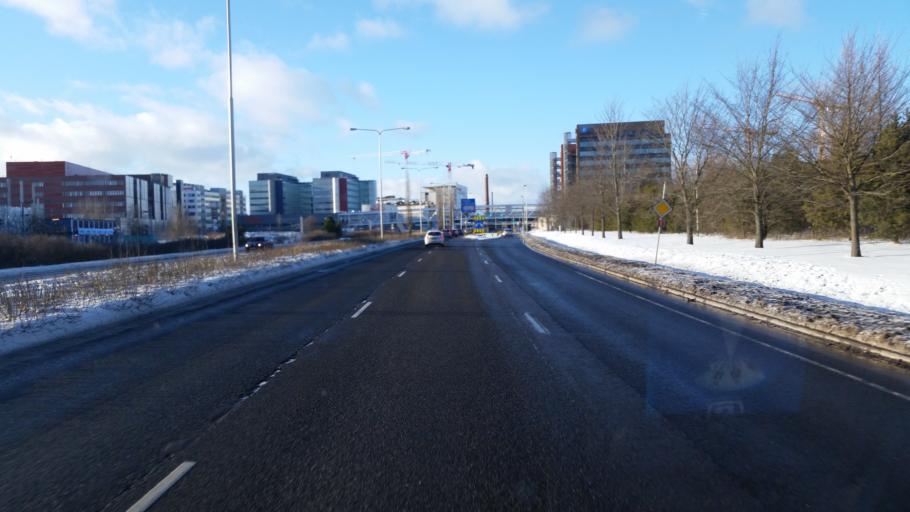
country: FI
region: Varsinais-Suomi
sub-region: Turku
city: Turku
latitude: 60.4477
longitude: 22.3023
